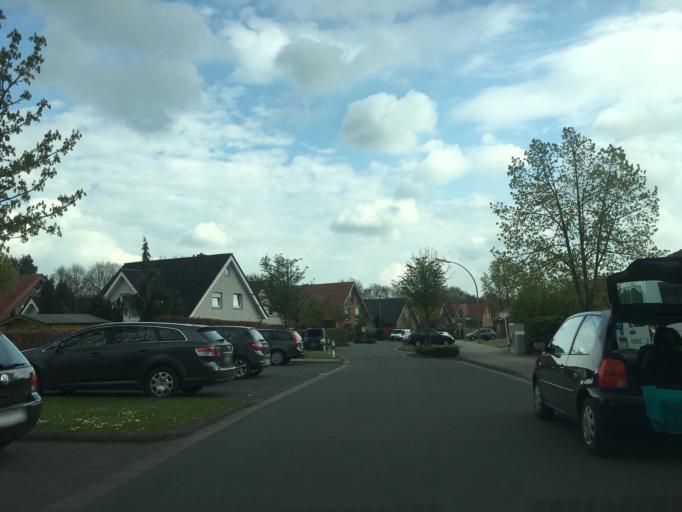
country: DE
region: North Rhine-Westphalia
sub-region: Regierungsbezirk Munster
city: Steinfurt
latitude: 52.1379
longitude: 7.3396
